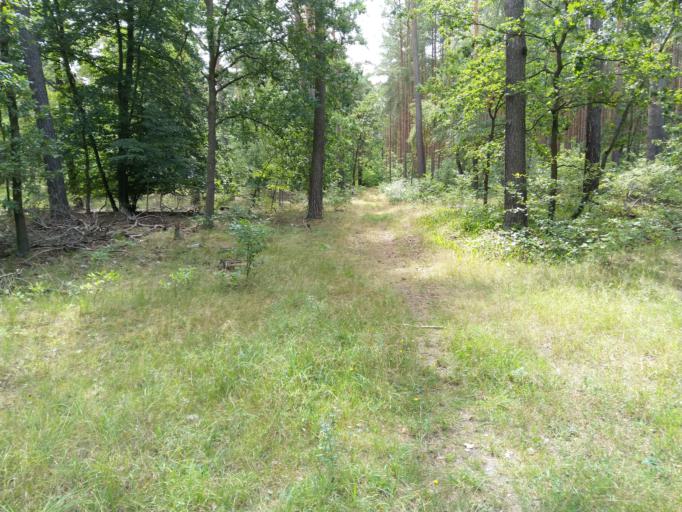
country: DE
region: Berlin
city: Rahnsdorf
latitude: 52.4493
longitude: 13.7135
